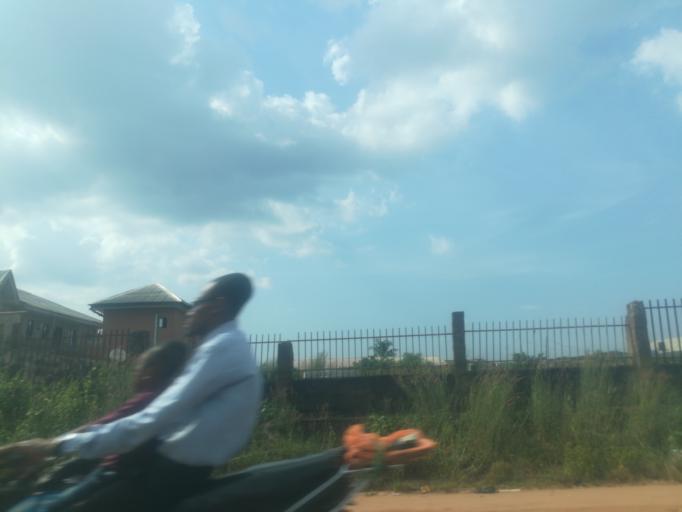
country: NG
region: Ogun
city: Abeokuta
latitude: 7.1136
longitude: 3.3140
